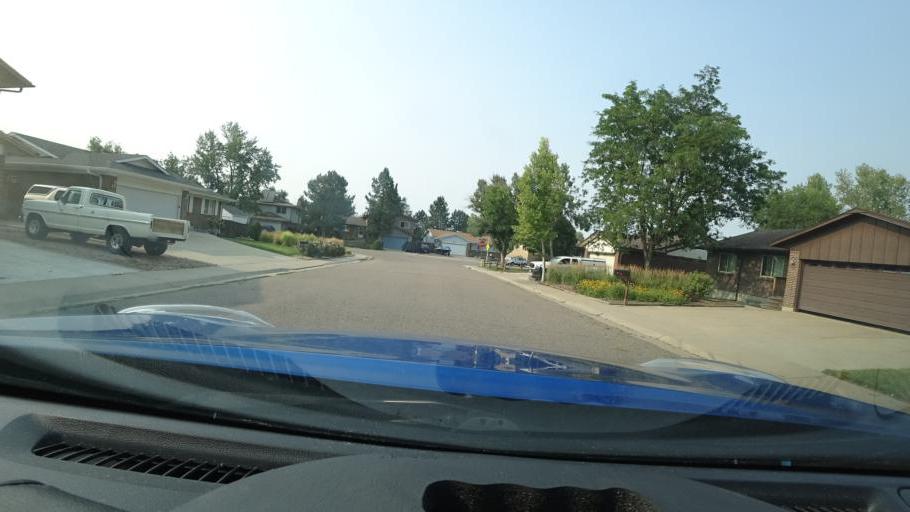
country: US
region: Colorado
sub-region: Adams County
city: Aurora
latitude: 39.6705
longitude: -104.7872
